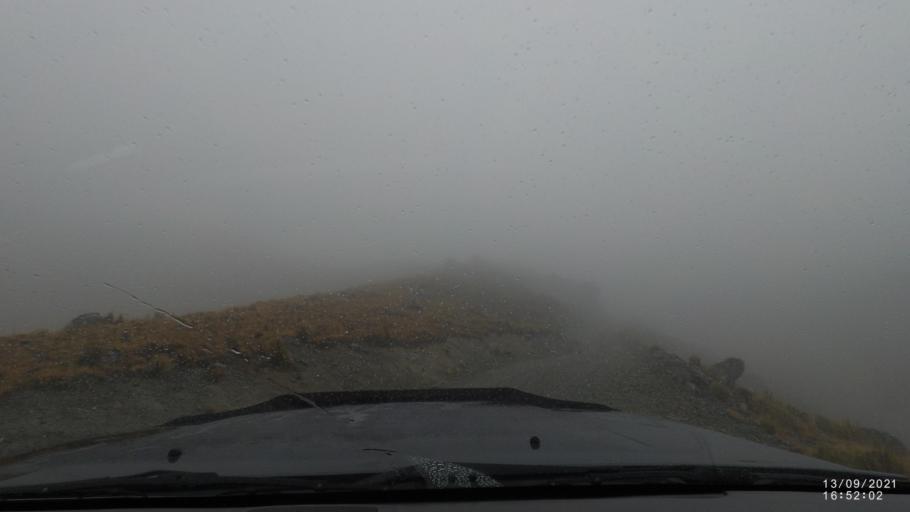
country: BO
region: Cochabamba
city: Colomi
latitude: -17.3066
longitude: -65.7066
